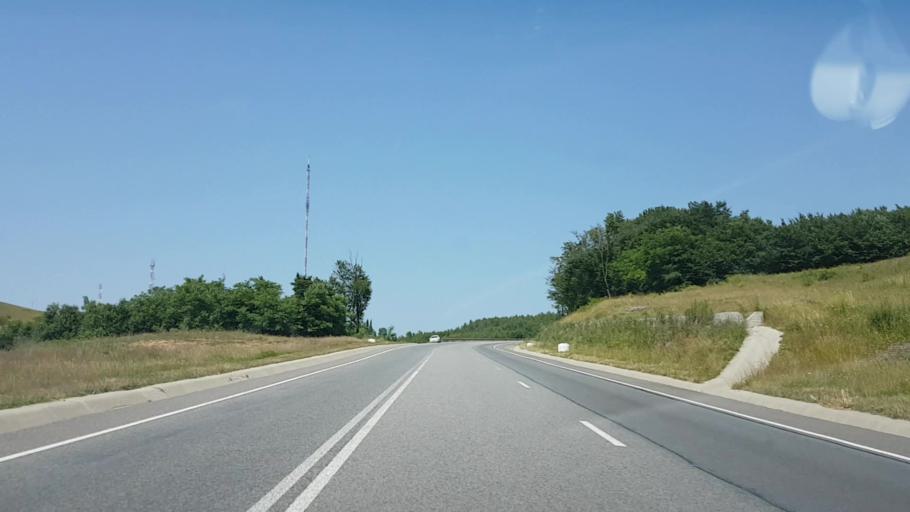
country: RO
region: Cluj
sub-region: Comuna Feleacu
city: Feleacu
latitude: 46.7047
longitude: 23.6422
